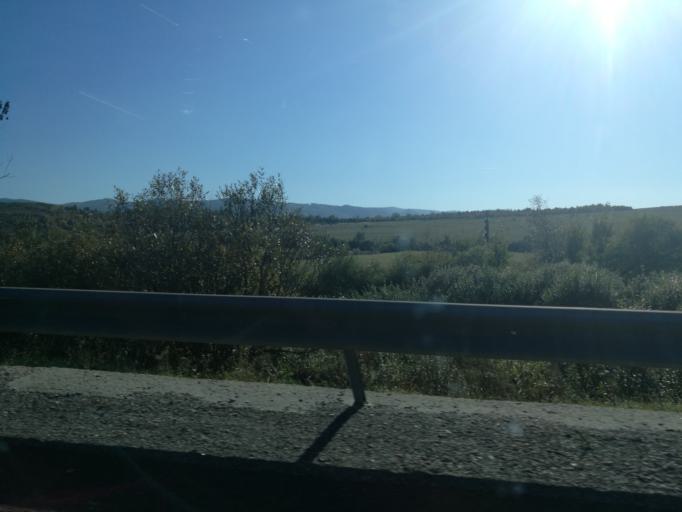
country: RO
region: Brasov
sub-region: Comuna Dumbravita
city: Dumbravita
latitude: 45.7718
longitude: 25.3540
